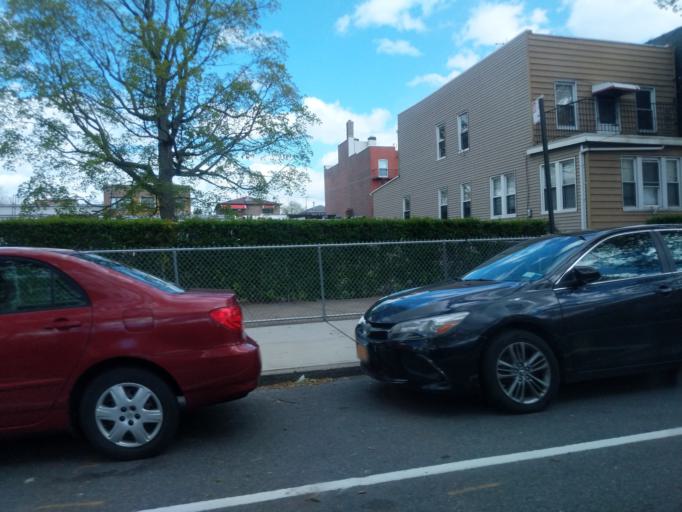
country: US
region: New York
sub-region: Bronx
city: The Bronx
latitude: 40.8720
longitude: -73.8613
